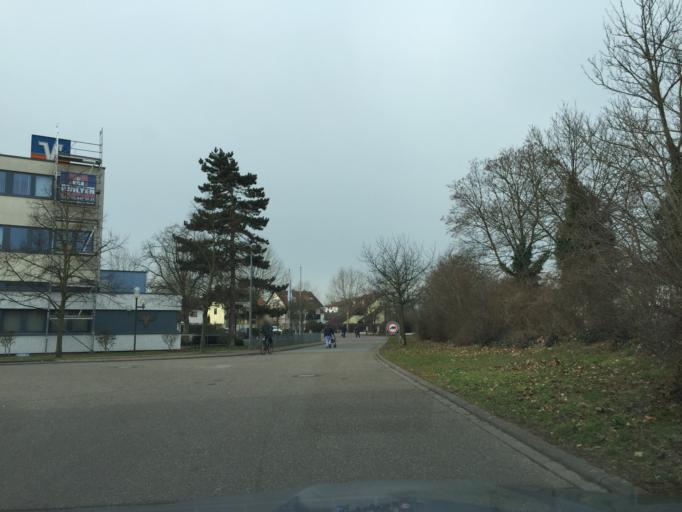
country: DE
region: Baden-Wuerttemberg
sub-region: Karlsruhe Region
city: Ketsch
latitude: 49.3699
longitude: 8.5313
